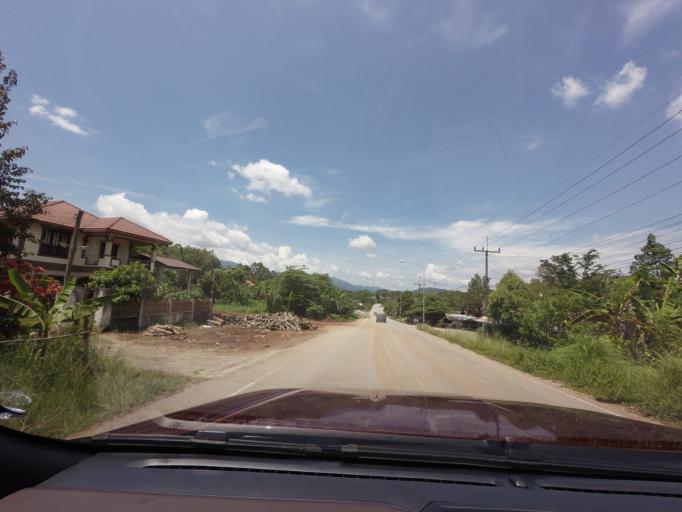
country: TH
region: Narathiwat
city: Chanae
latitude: 6.1812
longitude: 101.6979
